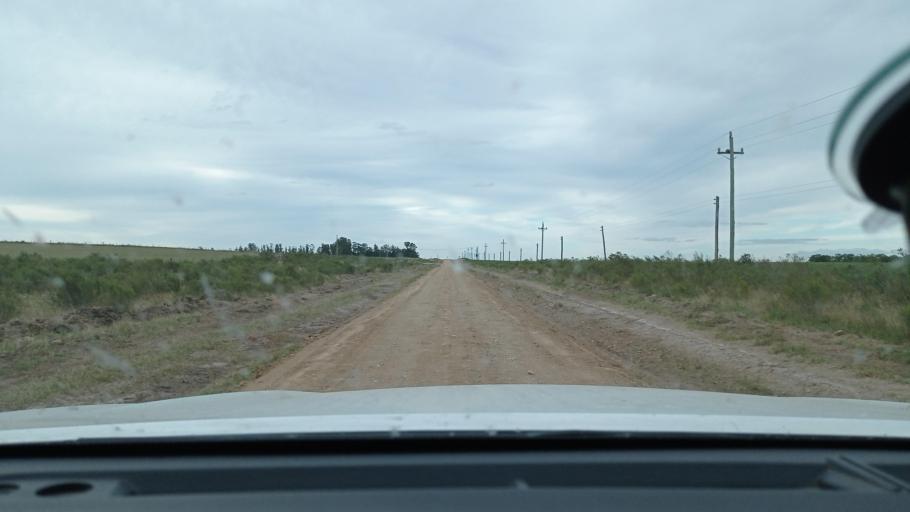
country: UY
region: Florida
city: Casupa
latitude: -34.1174
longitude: -55.7691
